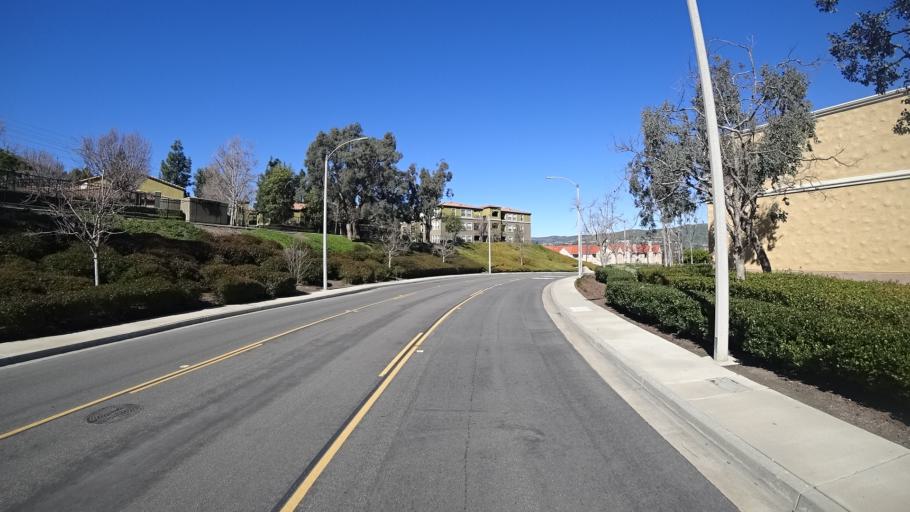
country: US
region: California
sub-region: Orange County
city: Yorba Linda
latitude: 33.8650
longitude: -117.7525
